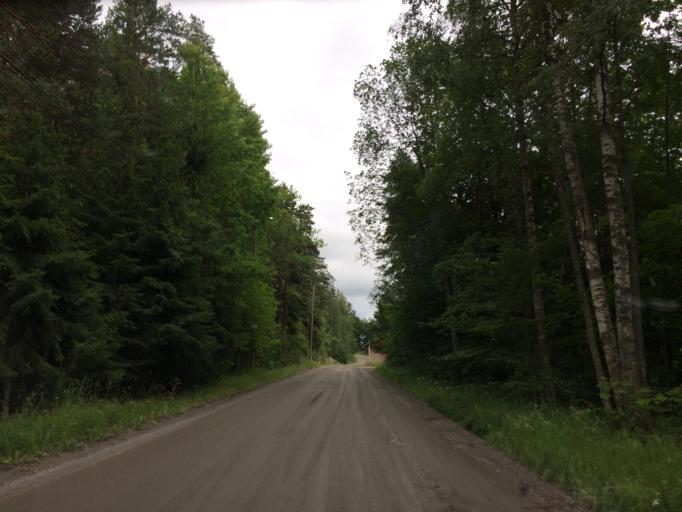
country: FI
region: Haeme
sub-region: Haemeenlinna
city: Haemeenlinna
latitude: 60.9694
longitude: 24.5209
